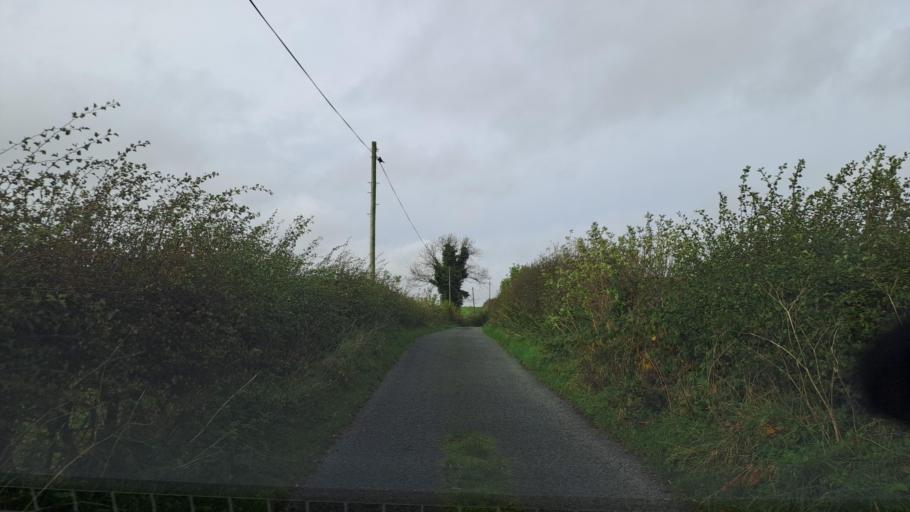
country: IE
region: Ulster
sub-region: County Monaghan
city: Carrickmacross
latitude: 54.0148
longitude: -6.8093
